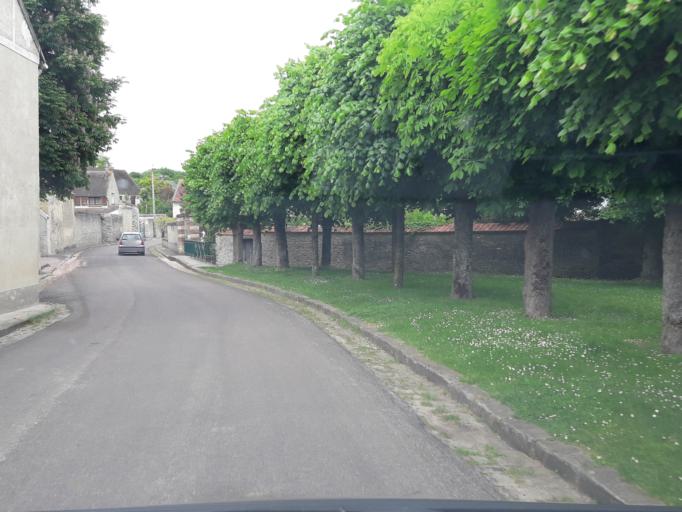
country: FR
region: Ile-de-France
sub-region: Departement de l'Essonne
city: Boissy-le-Cutte
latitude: 48.4048
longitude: 2.2630
